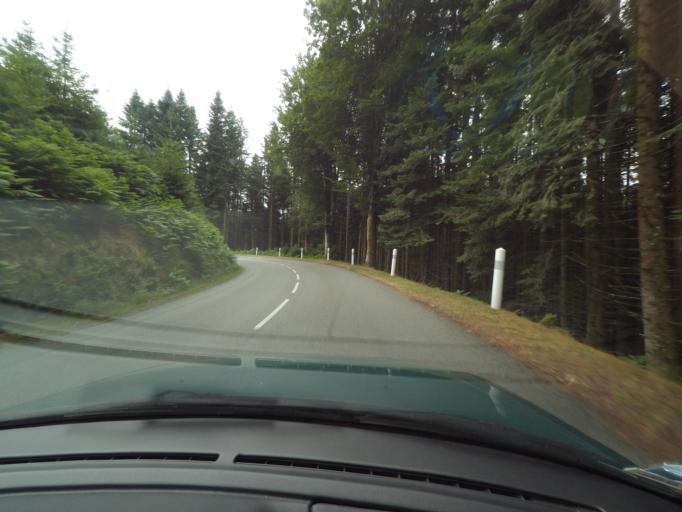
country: FR
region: Limousin
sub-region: Departement de la Haute-Vienne
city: Eymoutiers
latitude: 45.7236
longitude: 1.7868
